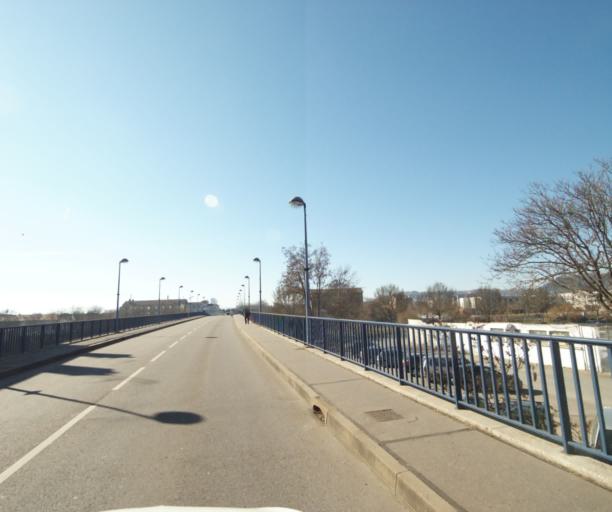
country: FR
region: Lorraine
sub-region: Departement de Meurthe-et-Moselle
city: Malzeville
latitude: 48.7065
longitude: 6.1846
